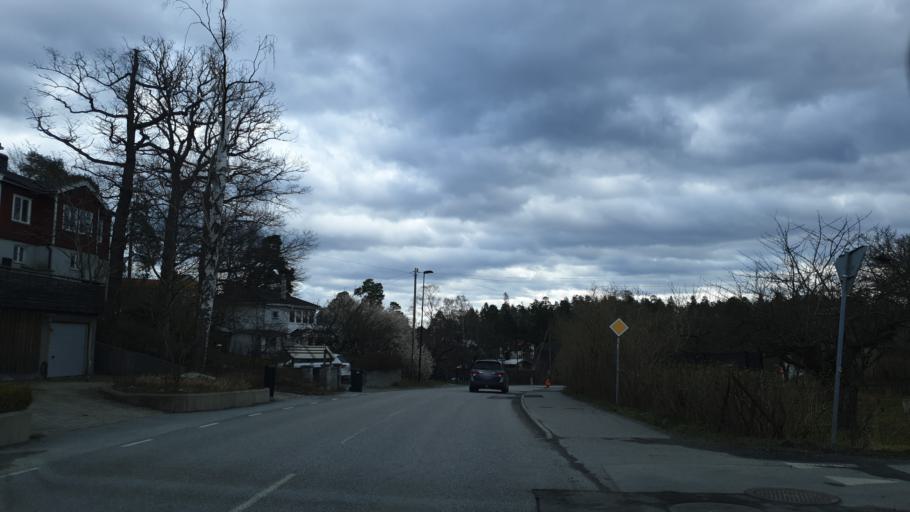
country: SE
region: Stockholm
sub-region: Nacka Kommun
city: Nacka
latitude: 59.3093
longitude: 18.2005
